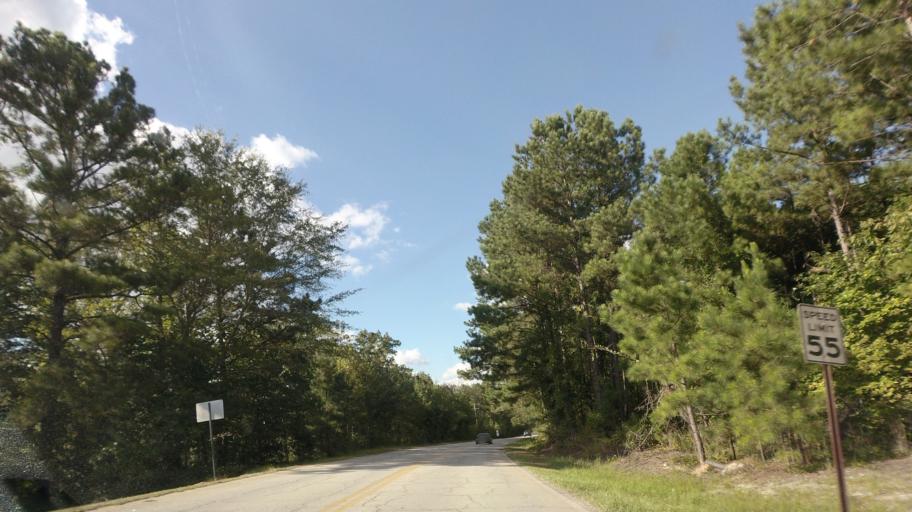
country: US
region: Georgia
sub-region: Lamar County
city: Barnesville
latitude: 33.0714
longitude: -84.1564
